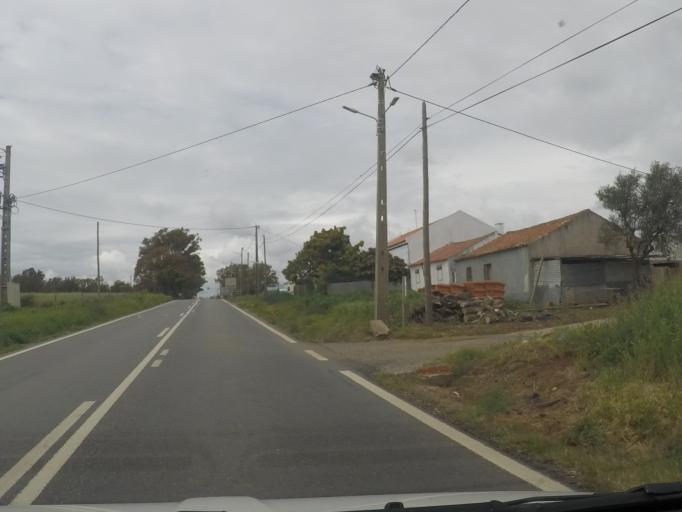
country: PT
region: Setubal
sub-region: Sines
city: Porto Covo
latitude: 37.8626
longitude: -8.7179
